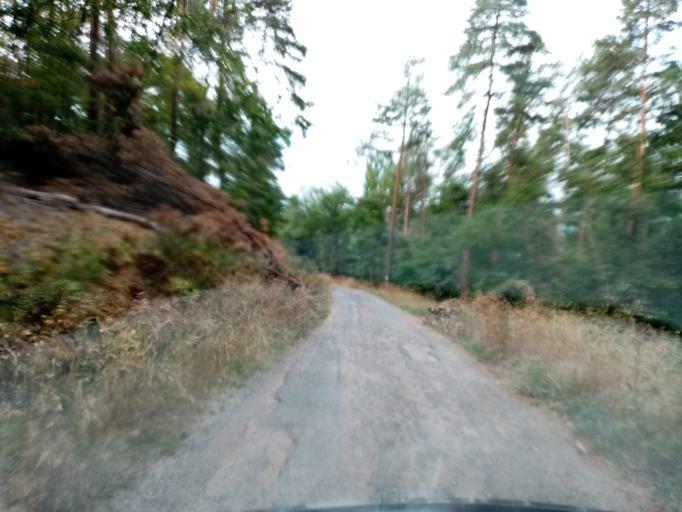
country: FR
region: Alsace
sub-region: Departement du Bas-Rhin
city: Andlau
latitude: 48.3539
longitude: 7.3734
